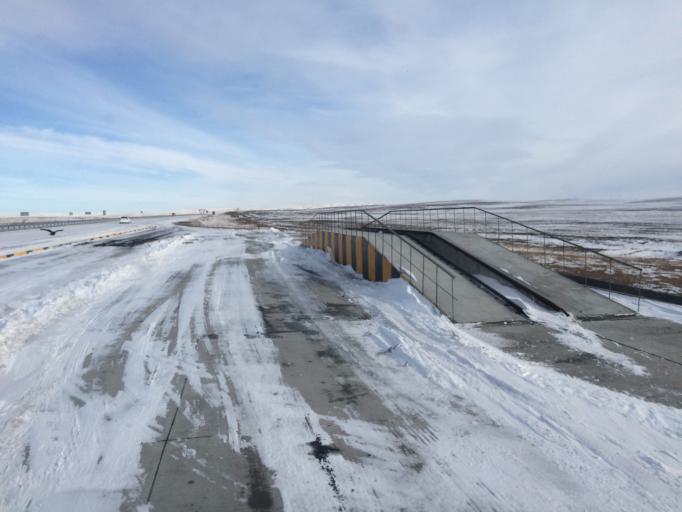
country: KZ
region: Zhambyl
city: Georgiyevka
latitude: 43.3683
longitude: 74.7289
